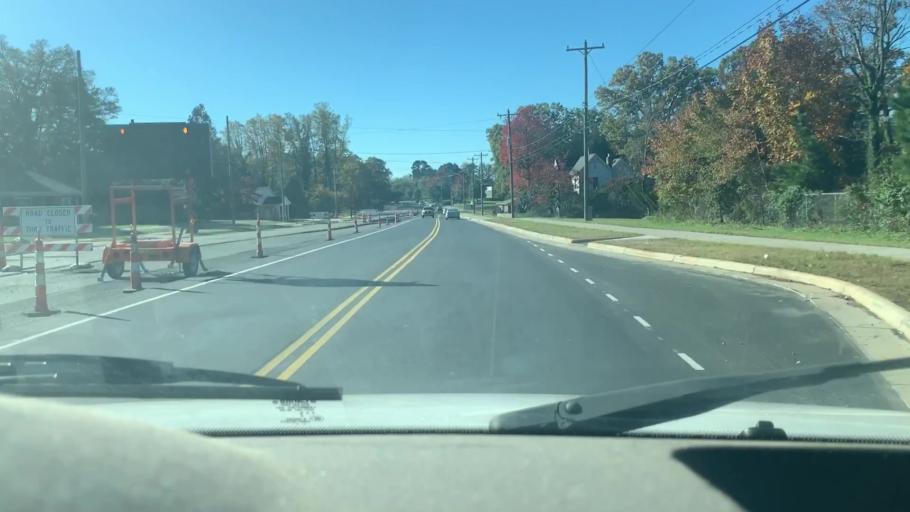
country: US
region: North Carolina
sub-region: Mecklenburg County
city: Charlotte
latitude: 35.2906
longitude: -80.8577
